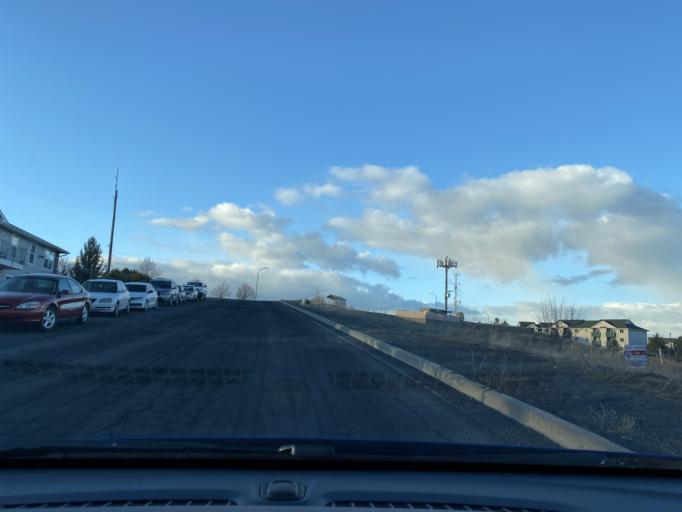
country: US
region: Washington
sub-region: Whitman County
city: Pullman
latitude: 46.7453
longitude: -117.1512
